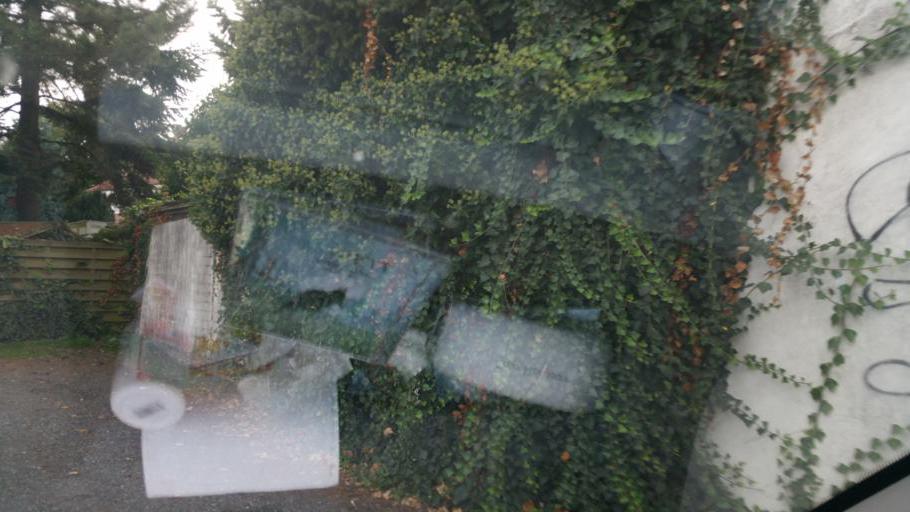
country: DE
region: North Rhine-Westphalia
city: Emsdetten
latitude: 52.1713
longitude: 7.5283
